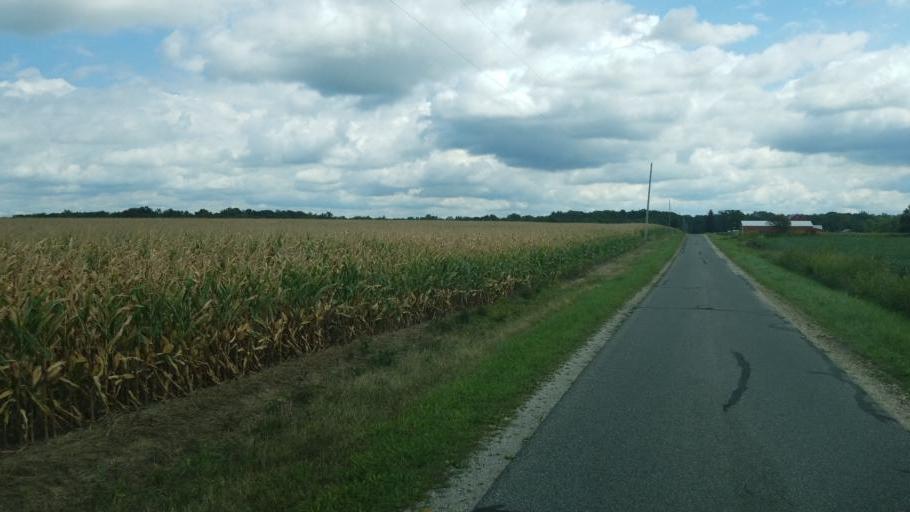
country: US
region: Ohio
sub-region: Huron County
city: Willard
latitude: 41.1155
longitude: -82.7824
